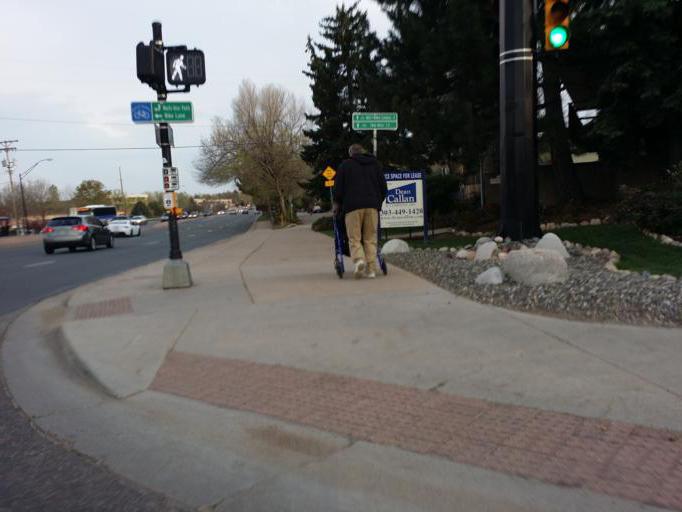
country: US
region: Colorado
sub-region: Boulder County
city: Boulder
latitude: 40.0000
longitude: -105.2639
